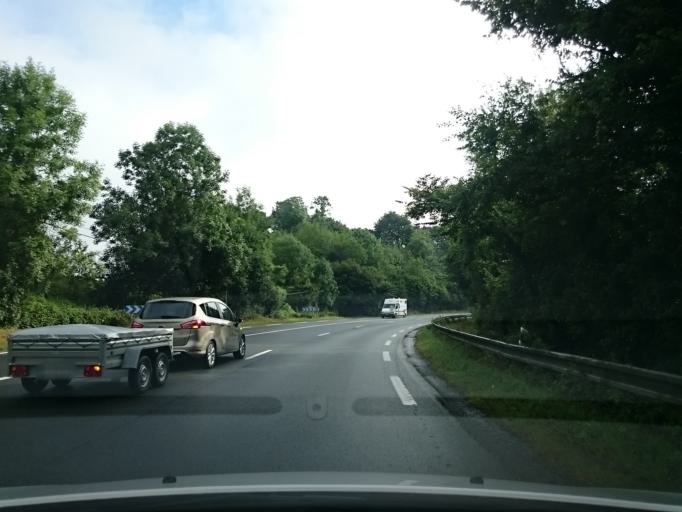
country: FR
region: Lower Normandy
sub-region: Departement du Calvados
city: Cambremer
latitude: 49.1283
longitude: 0.1061
